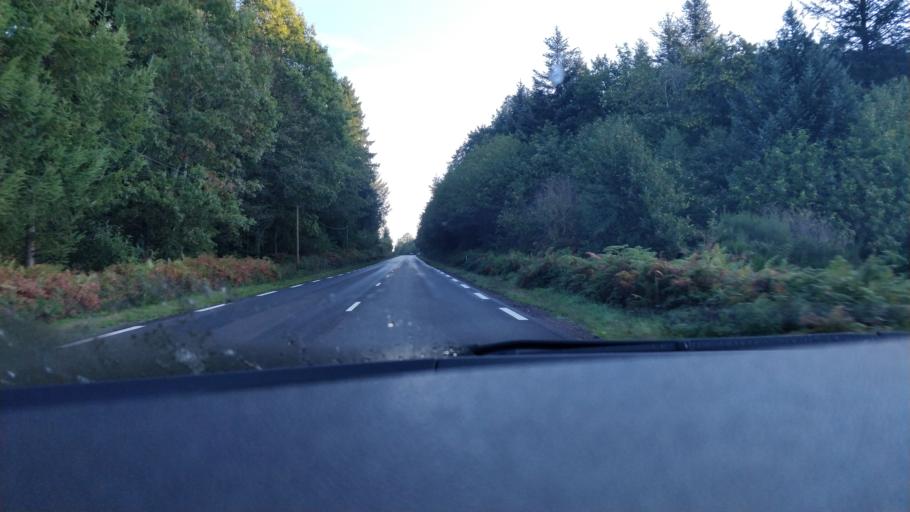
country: FR
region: Limousin
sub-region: Departement de la Haute-Vienne
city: Saint-Leonard-de-Noblat
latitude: 45.8719
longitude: 1.5359
